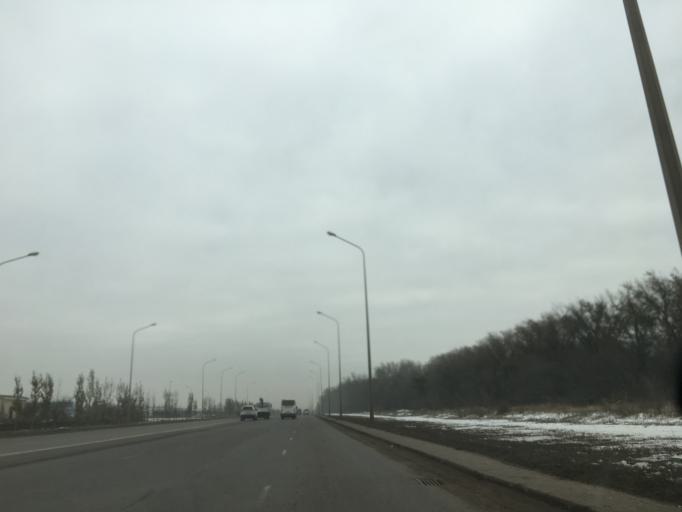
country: KZ
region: Astana Qalasy
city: Astana
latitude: 51.1692
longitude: 71.4949
